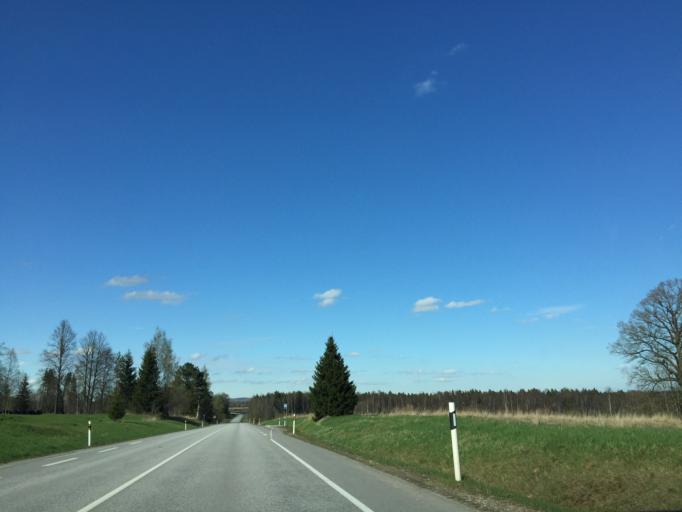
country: EE
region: Vorumaa
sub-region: Antsla vald
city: Vana-Antsla
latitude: 57.8839
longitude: 26.2833
